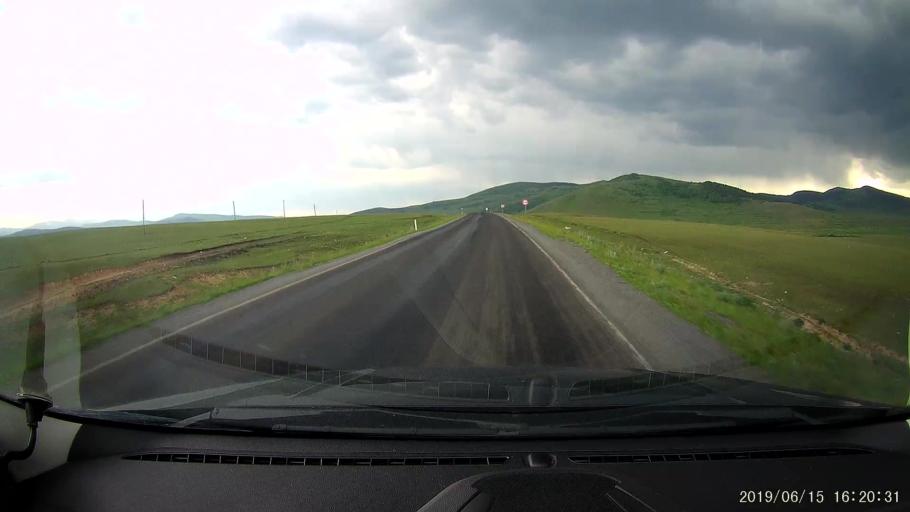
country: TR
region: Ardahan
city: Hanak
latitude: 41.2129
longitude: 42.8473
